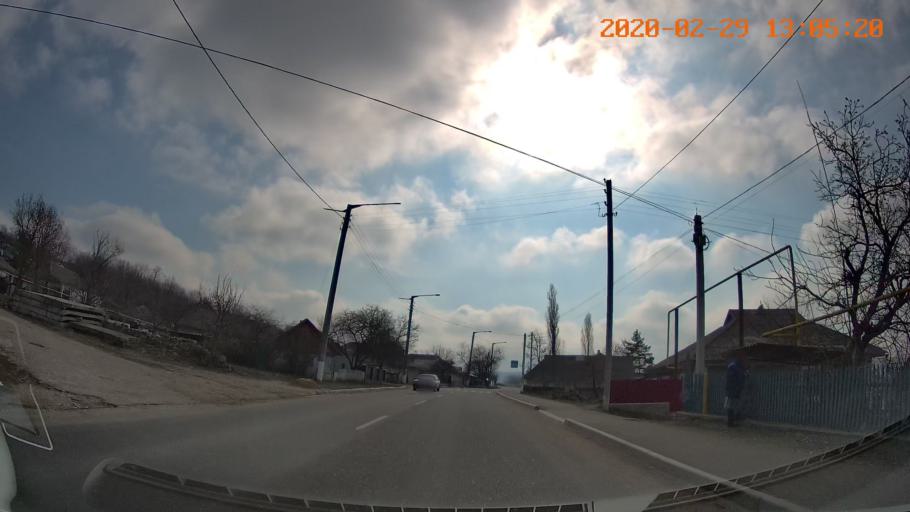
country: MD
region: Telenesti
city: Camenca
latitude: 48.0212
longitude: 28.7077
